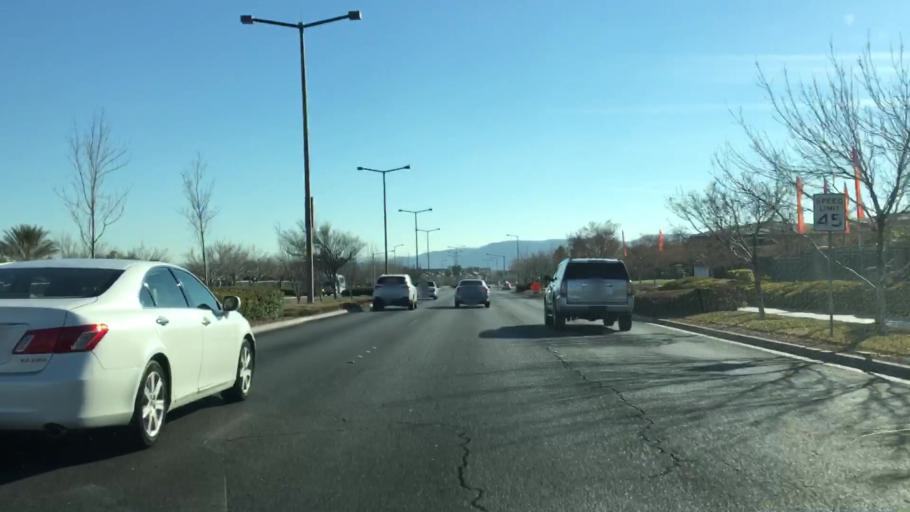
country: US
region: Nevada
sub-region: Clark County
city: Summerlin South
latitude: 36.1292
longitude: -115.3247
